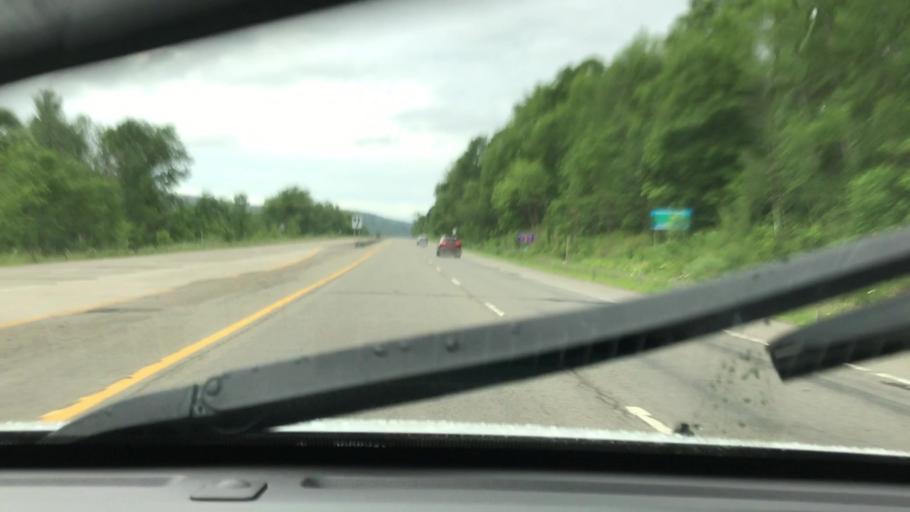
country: US
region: Pennsylvania
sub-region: McKean County
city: Foster Brook
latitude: 42.0049
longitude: -78.6208
